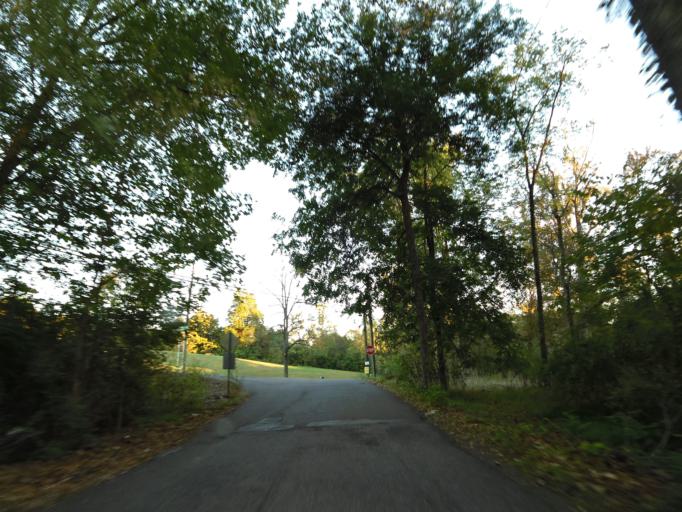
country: US
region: Tennessee
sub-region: Knox County
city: Knoxville
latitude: 36.0297
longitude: -83.9741
